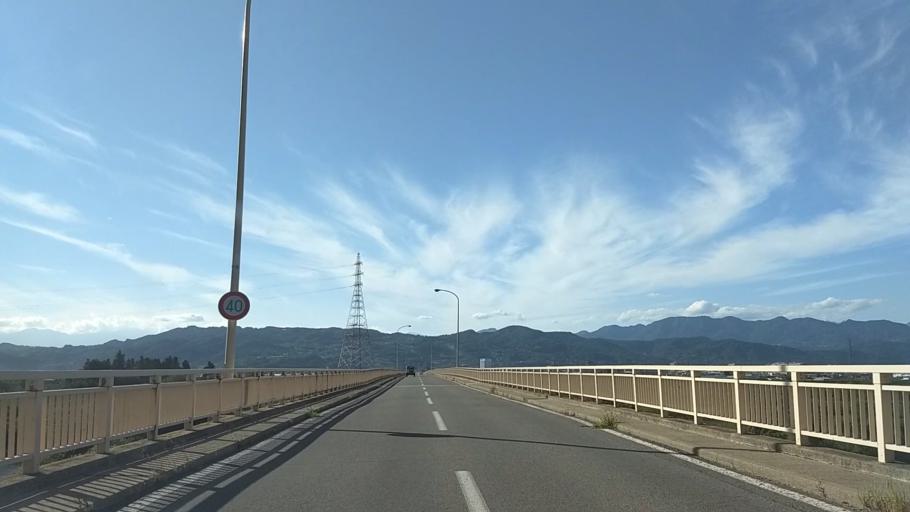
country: JP
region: Nagano
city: Nagano-shi
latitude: 36.5614
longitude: 138.1589
